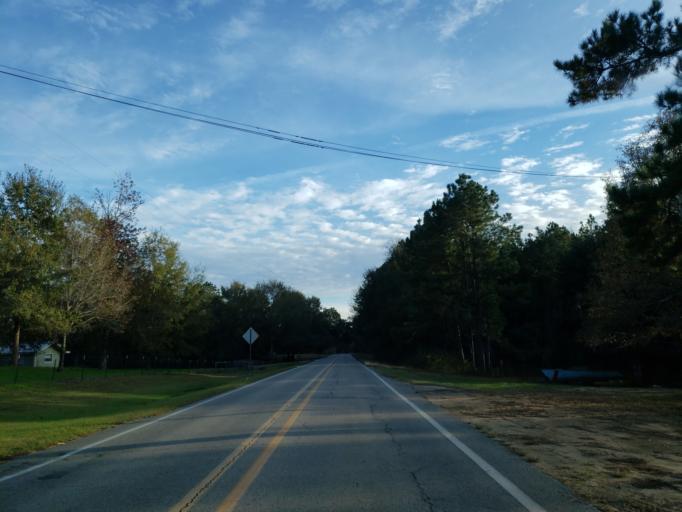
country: US
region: Mississippi
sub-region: Lamar County
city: Purvis
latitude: 31.1786
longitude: -89.4340
